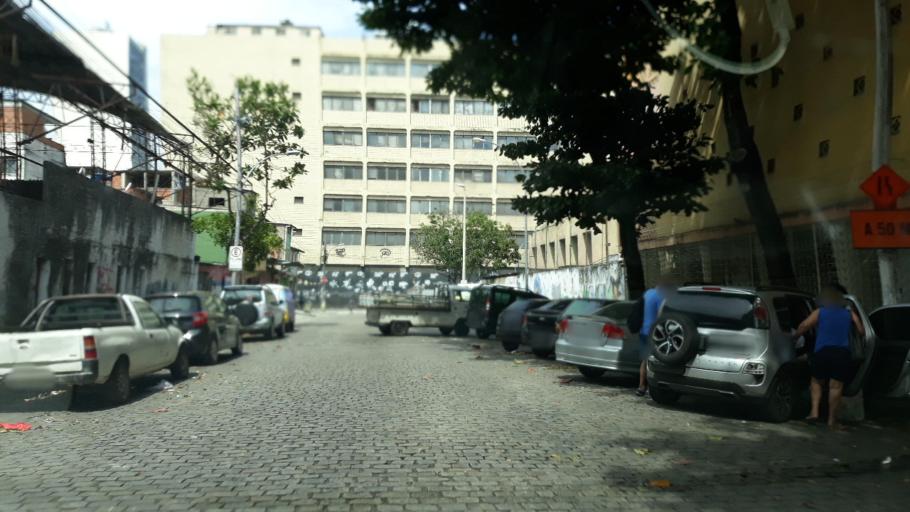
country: BR
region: Rio de Janeiro
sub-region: Rio De Janeiro
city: Rio de Janeiro
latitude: -22.9071
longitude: -43.1933
